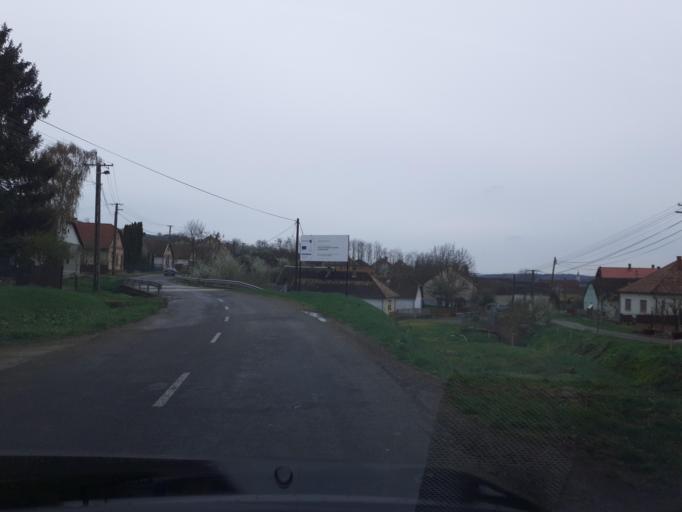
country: HU
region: Tolna
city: Hogyesz
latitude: 46.4233
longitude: 18.4532
